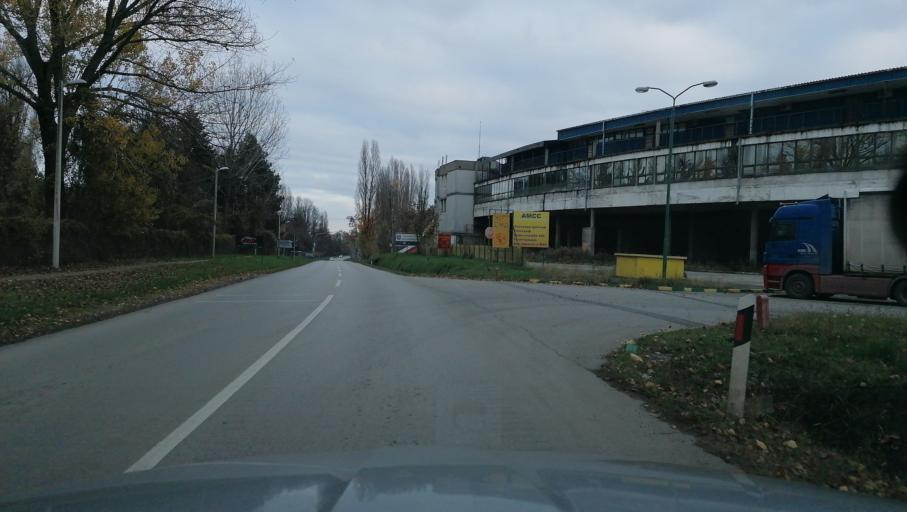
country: RS
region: Central Serbia
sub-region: Podunavski Okrug
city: Smederevo
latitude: 44.6612
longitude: 20.9006
